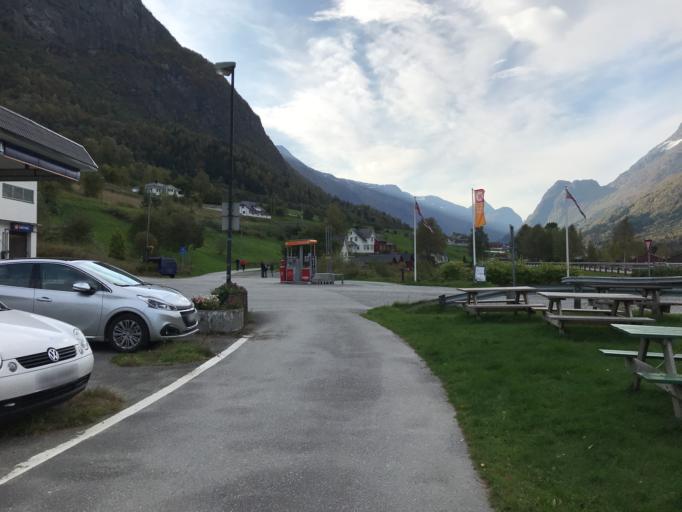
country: NO
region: Sogn og Fjordane
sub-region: Stryn
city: Stryn
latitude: 61.8418
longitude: 6.8109
